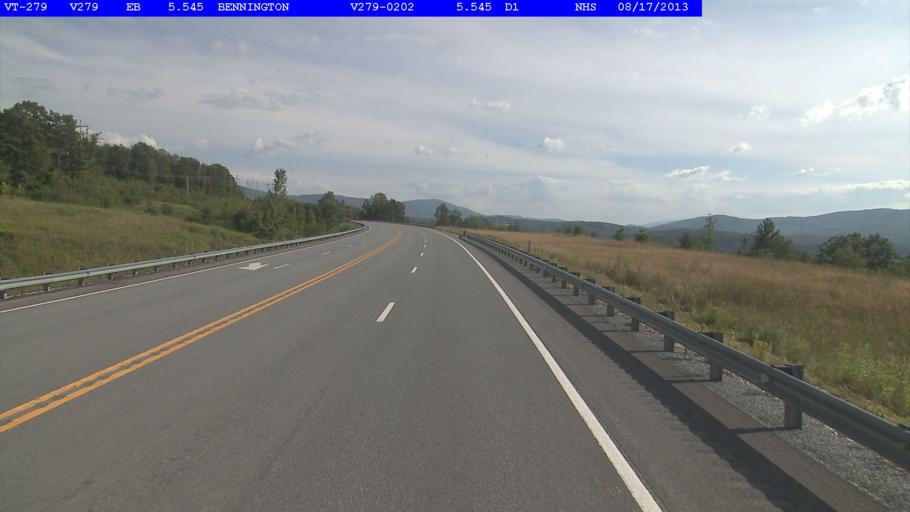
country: US
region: Vermont
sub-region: Bennington County
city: Bennington
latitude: 42.8938
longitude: -73.1768
